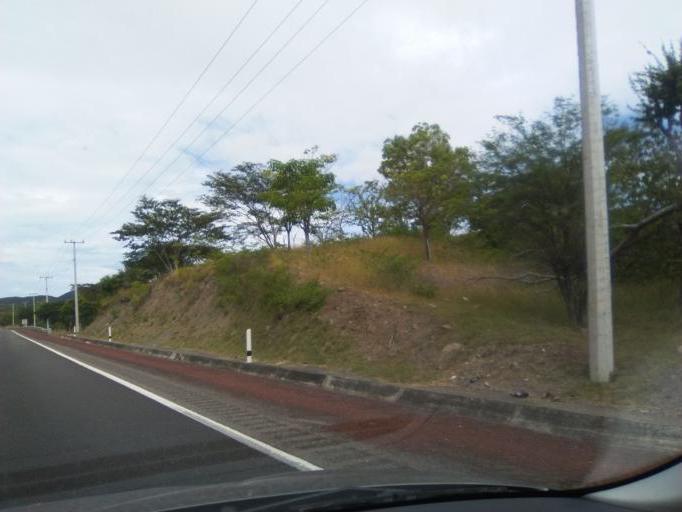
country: MX
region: Guerrero
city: Zumpango del Rio
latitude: 17.6544
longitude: -99.5011
